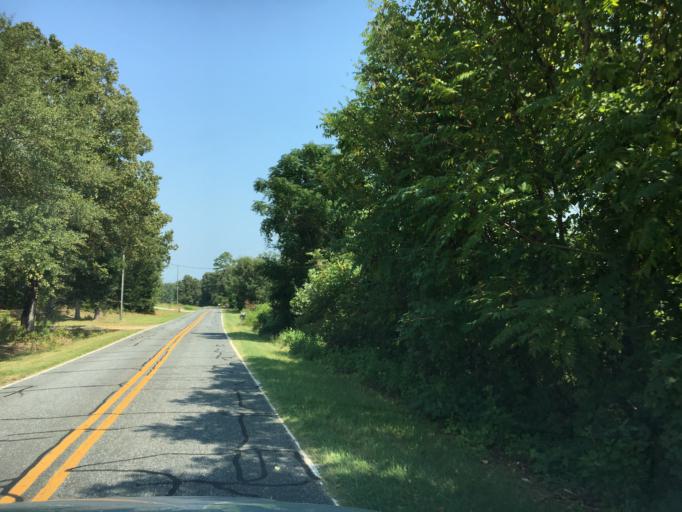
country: US
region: South Carolina
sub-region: Spartanburg County
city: Mayo
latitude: 35.1865
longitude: -81.9252
